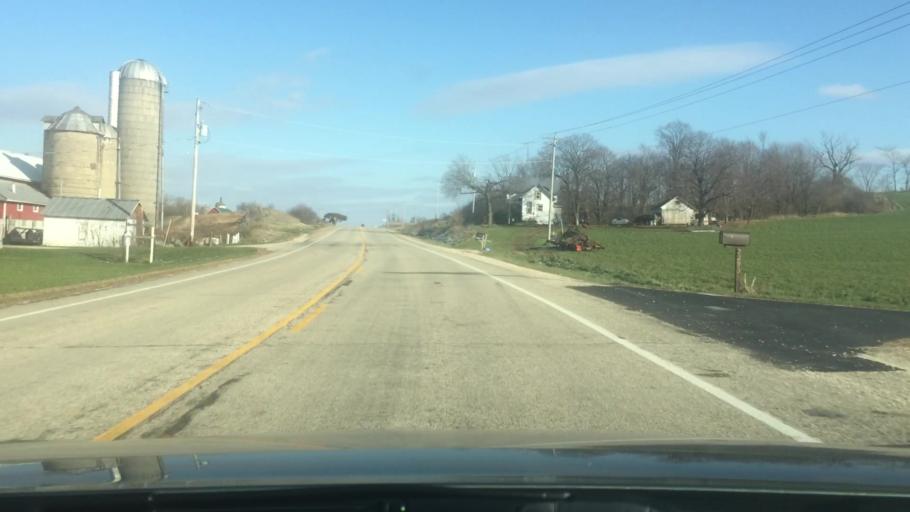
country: US
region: Wisconsin
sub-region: Jefferson County
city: Palmyra
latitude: 42.9326
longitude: -88.6504
